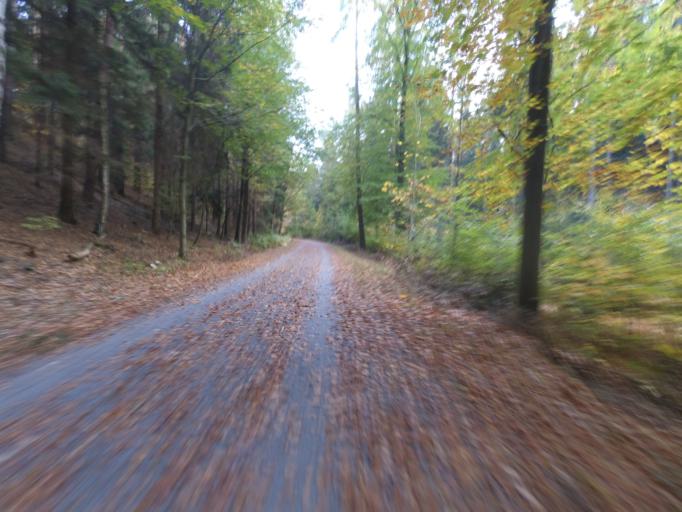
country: DE
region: Saxony
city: Albertstadt
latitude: 51.0946
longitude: 13.8310
